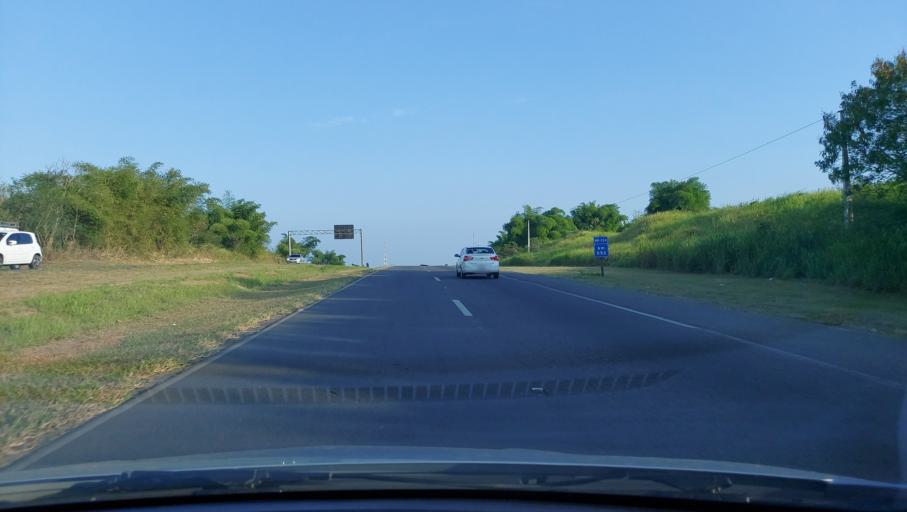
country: BR
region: Bahia
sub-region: Santo Amaro
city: Santo Amaro
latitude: -12.4575
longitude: -38.7006
